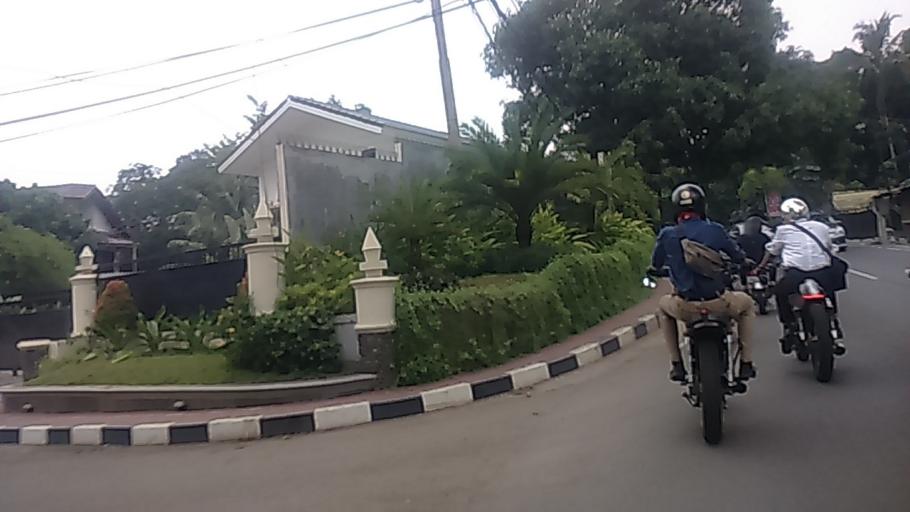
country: ID
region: West Java
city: Pamulang
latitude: -6.3040
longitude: 106.7739
